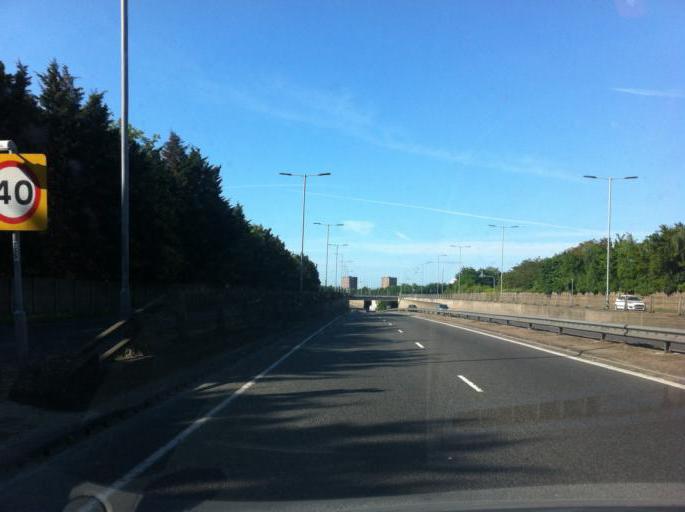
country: GB
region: England
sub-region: Greater London
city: Hayes
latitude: 51.5189
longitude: -0.3984
